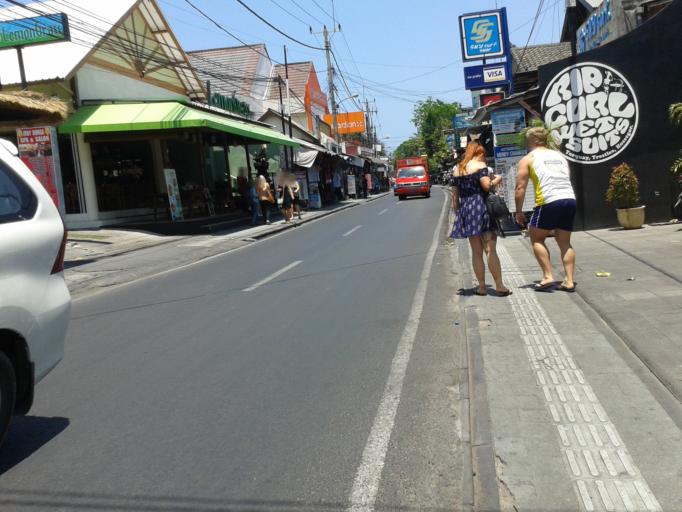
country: ID
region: Bali
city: Kuta
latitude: -8.7083
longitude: 115.1713
